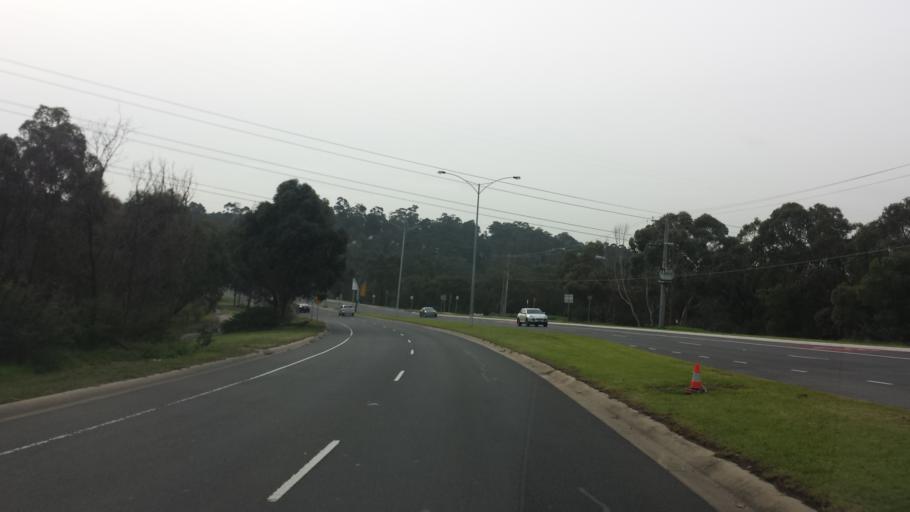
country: AU
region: Victoria
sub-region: Nillumbik
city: Eltham
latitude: -37.7436
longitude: 145.1365
